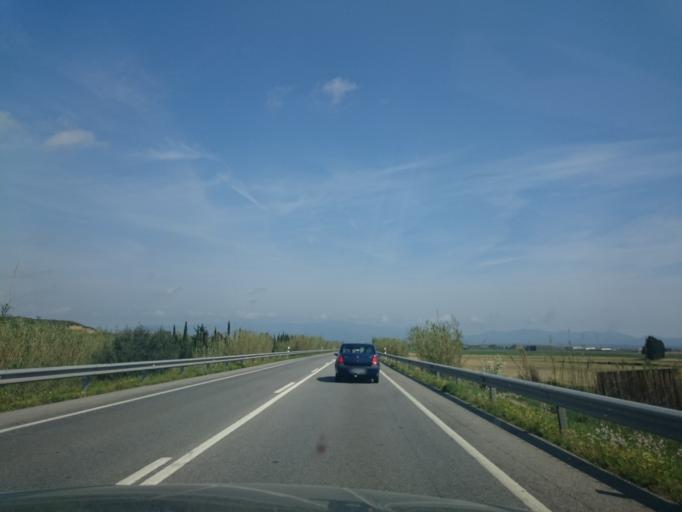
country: ES
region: Catalonia
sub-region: Provincia de Girona
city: Figueres
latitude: 42.2495
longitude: 2.9844
